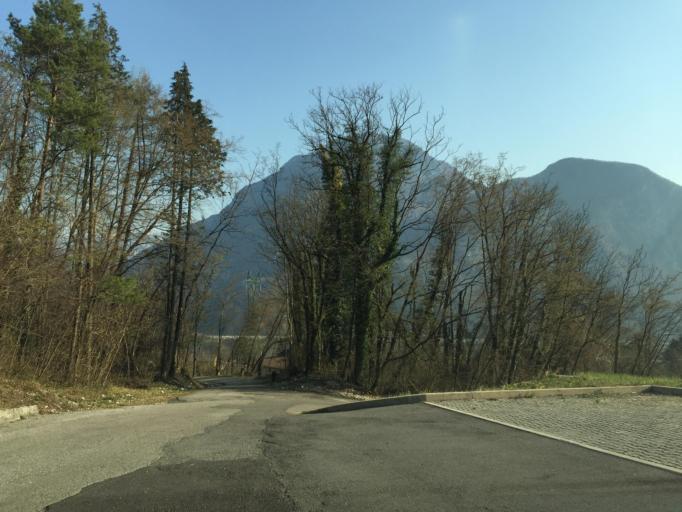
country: IT
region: Friuli Venezia Giulia
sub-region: Provincia di Udine
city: Amaro
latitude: 46.3781
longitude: 13.0919
